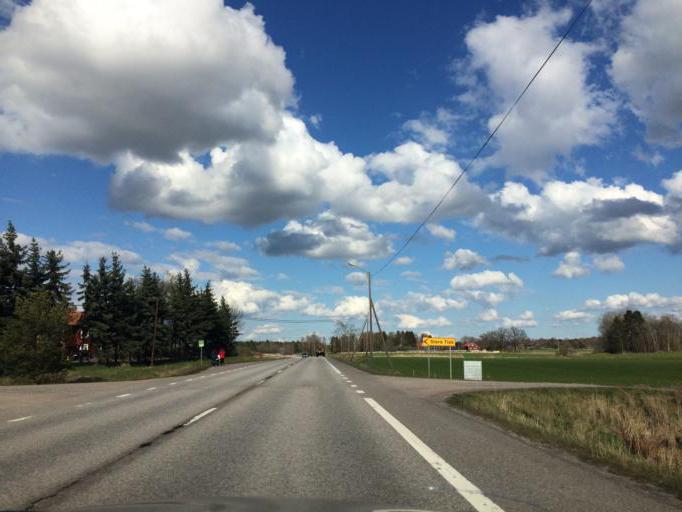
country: SE
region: Soedermanland
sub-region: Eskilstuna Kommun
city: Eskilstuna
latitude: 59.4027
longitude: 16.5664
